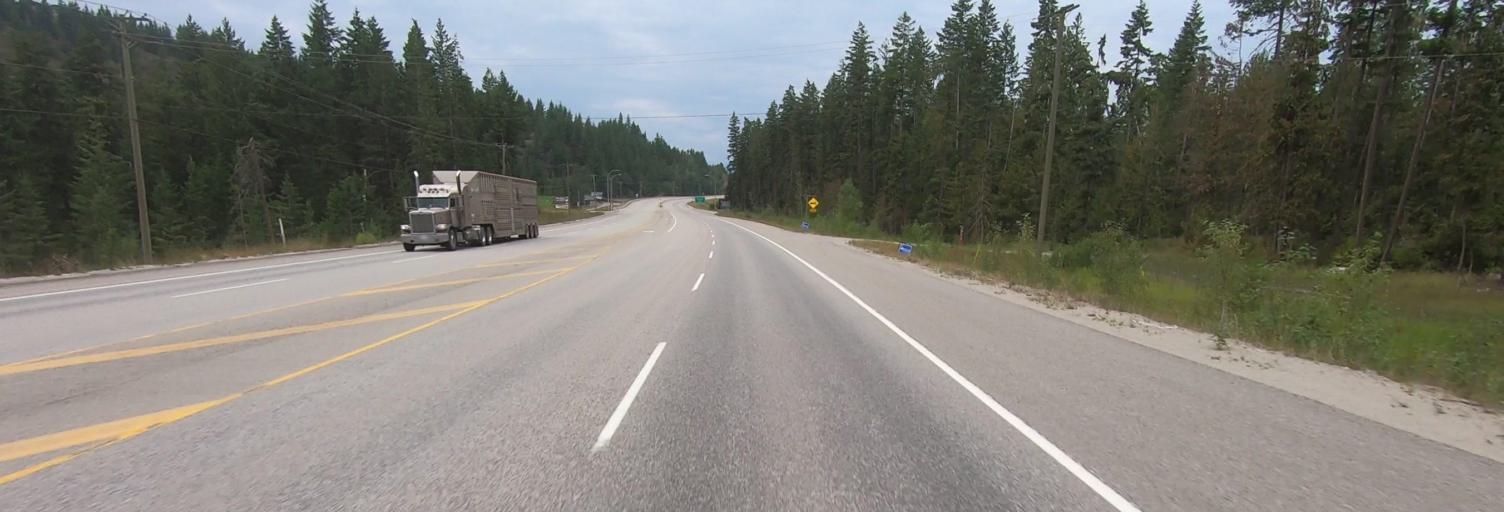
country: CA
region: British Columbia
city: Salmon Arm
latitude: 50.8637
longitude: -119.3749
